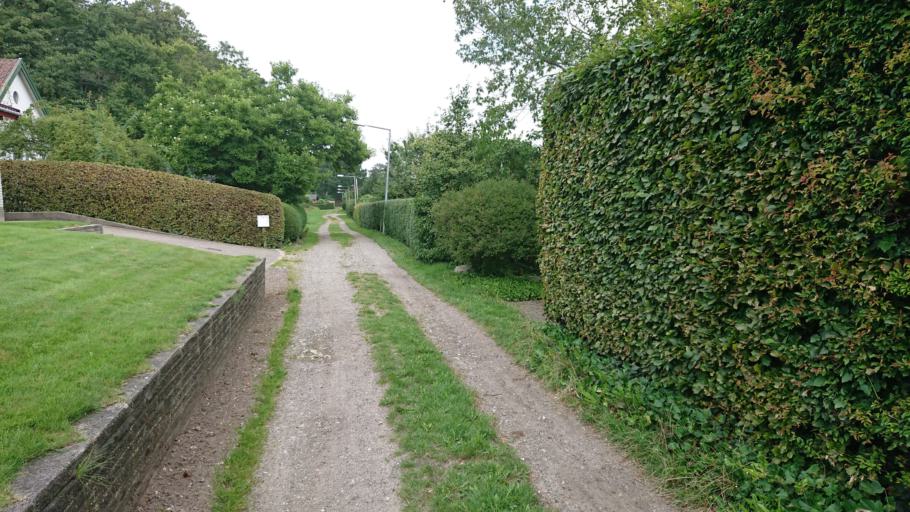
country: DK
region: North Denmark
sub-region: Frederikshavn Kommune
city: Saeby
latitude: 57.3408
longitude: 10.5098
